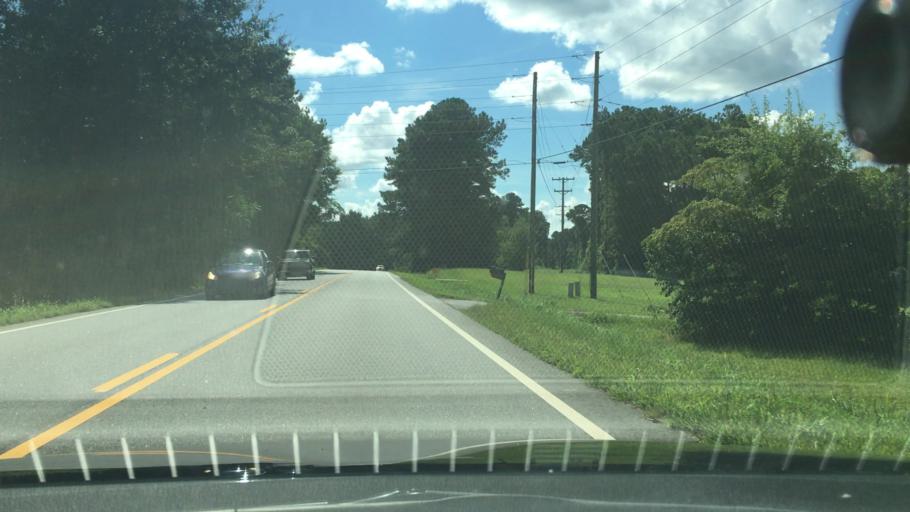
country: US
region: Georgia
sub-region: Butts County
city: Jackson
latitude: 33.2884
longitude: -83.9246
